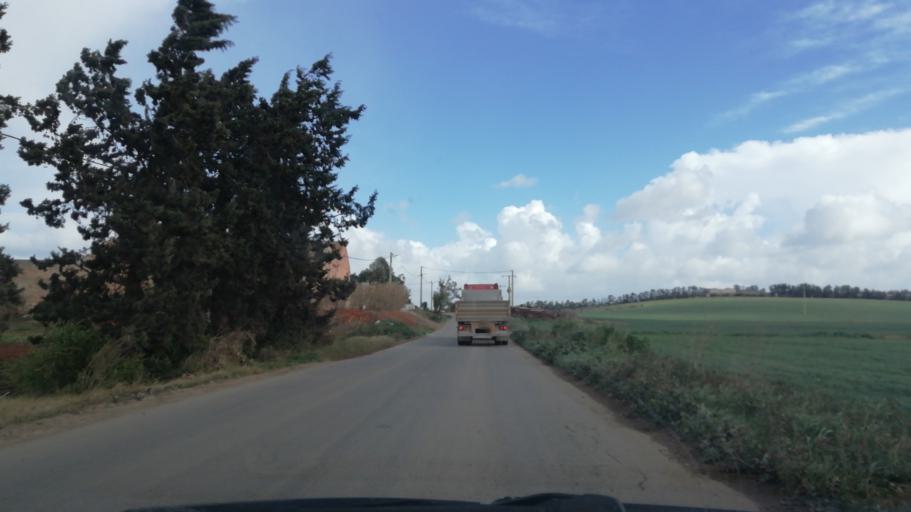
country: DZ
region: Oran
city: Sidi ech Chahmi
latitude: 35.6413
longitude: -0.5172
